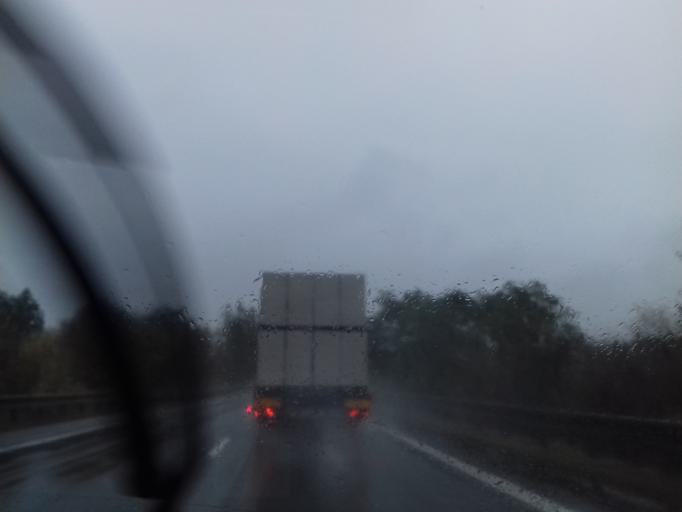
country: CZ
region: Pardubicky
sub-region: Okres Svitavy
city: Svitavy
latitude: 49.7958
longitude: 16.4625
